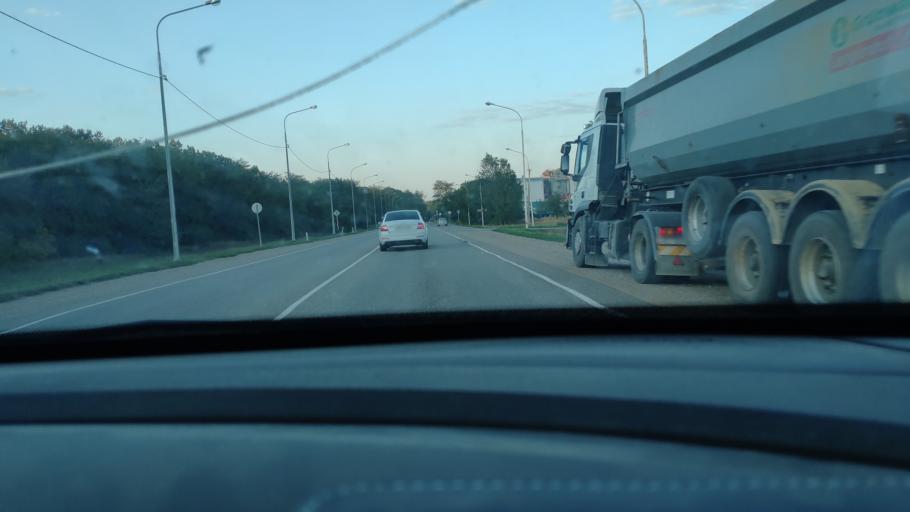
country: RU
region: Krasnodarskiy
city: Novominskaya
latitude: 46.3204
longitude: 38.9326
